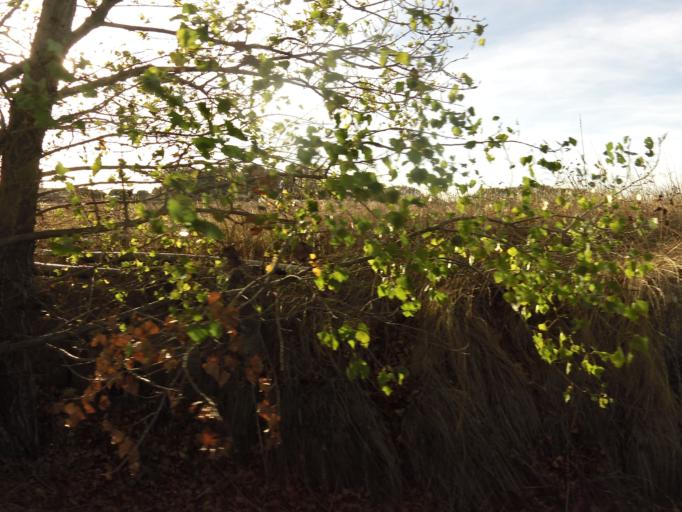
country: FR
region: Languedoc-Roussillon
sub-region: Departement du Gard
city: Aimargues
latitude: 43.6907
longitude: 4.2140
